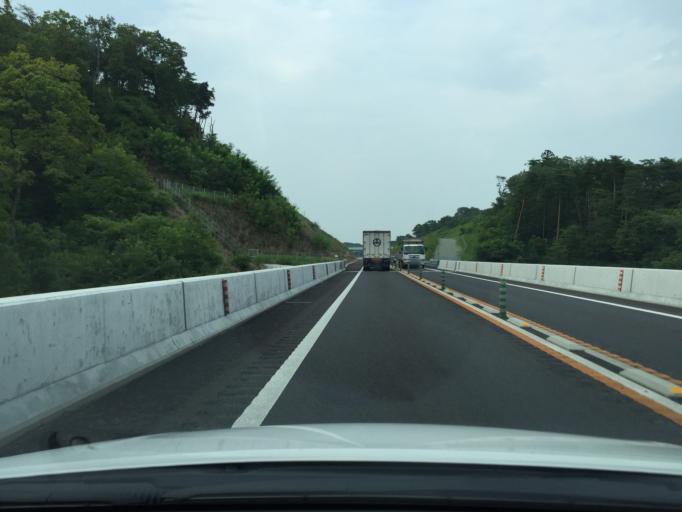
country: JP
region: Fukushima
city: Namie
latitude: 37.4523
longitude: 140.9606
